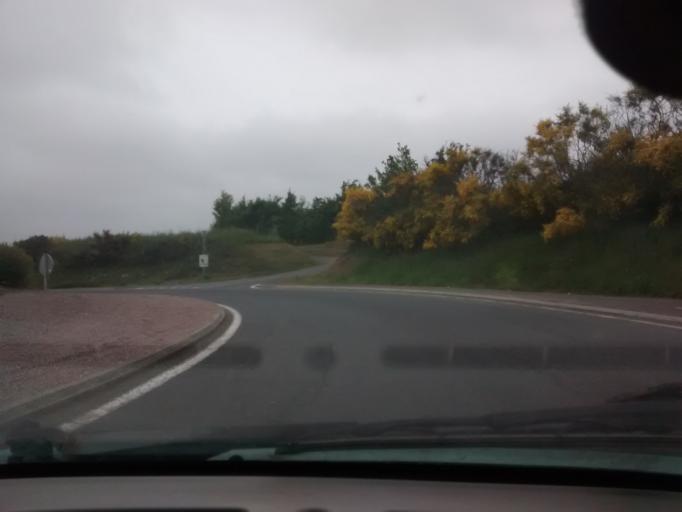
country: FR
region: Lower Normandy
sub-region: Departement de la Manche
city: Torigni-sur-Vire
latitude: 49.0489
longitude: -1.0021
